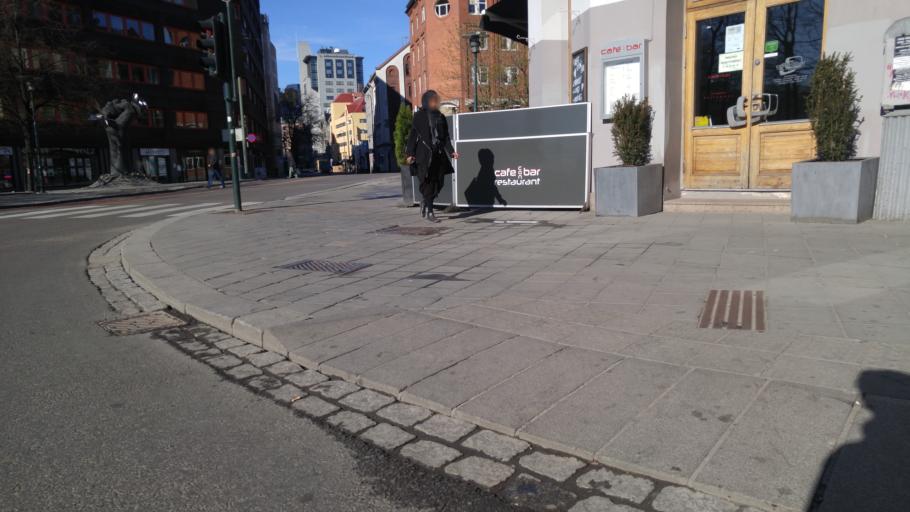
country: NO
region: Oslo
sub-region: Oslo
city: Oslo
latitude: 59.9138
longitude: 10.7568
